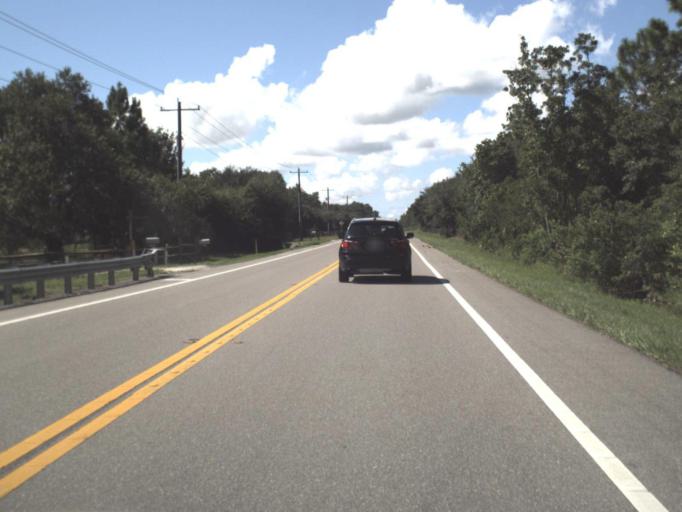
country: US
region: Florida
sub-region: Sarasota County
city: Lake Sarasota
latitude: 27.3881
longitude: -82.2807
